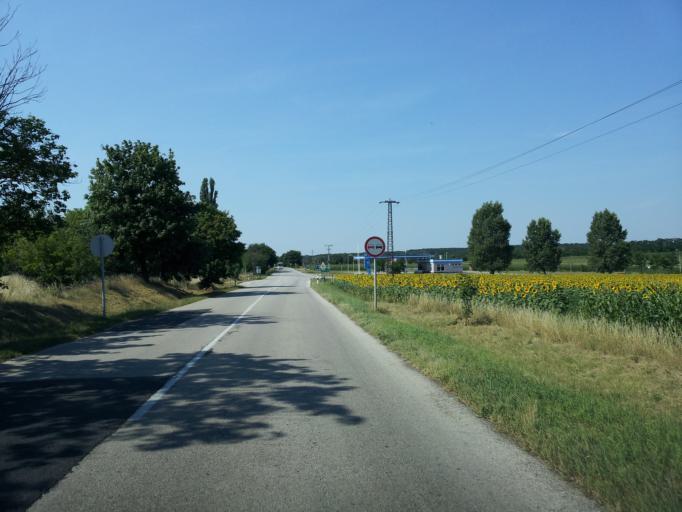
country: HU
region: Fejer
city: Pakozd
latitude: 47.2593
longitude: 18.5184
